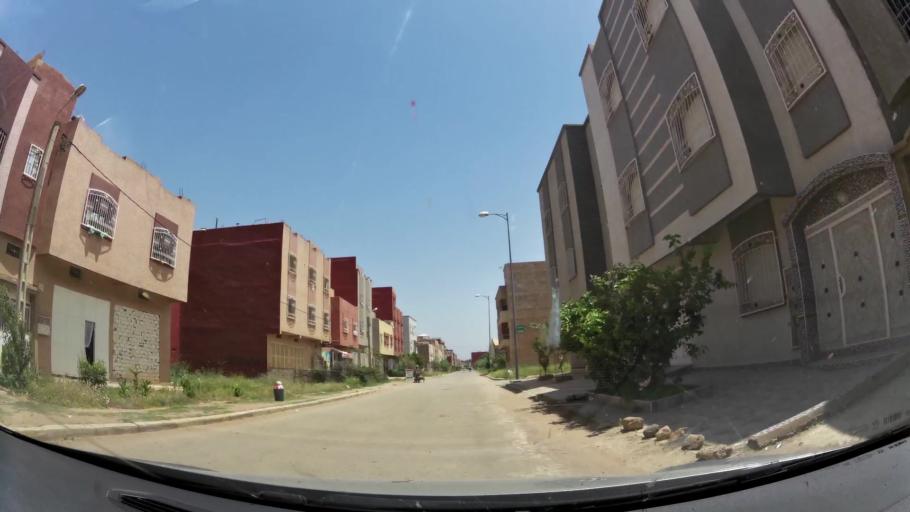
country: MA
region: Rabat-Sale-Zemmour-Zaer
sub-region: Khemisset
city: Khemisset
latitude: 33.8246
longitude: -6.0837
